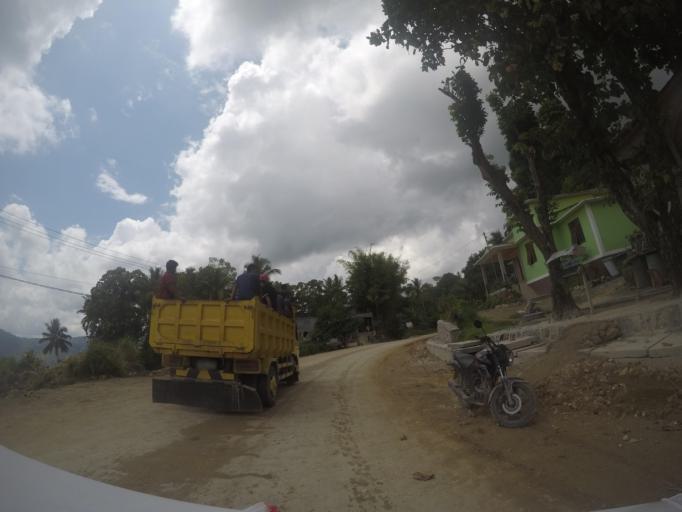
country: TL
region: Baucau
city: Venilale
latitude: -8.6003
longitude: 126.3859
